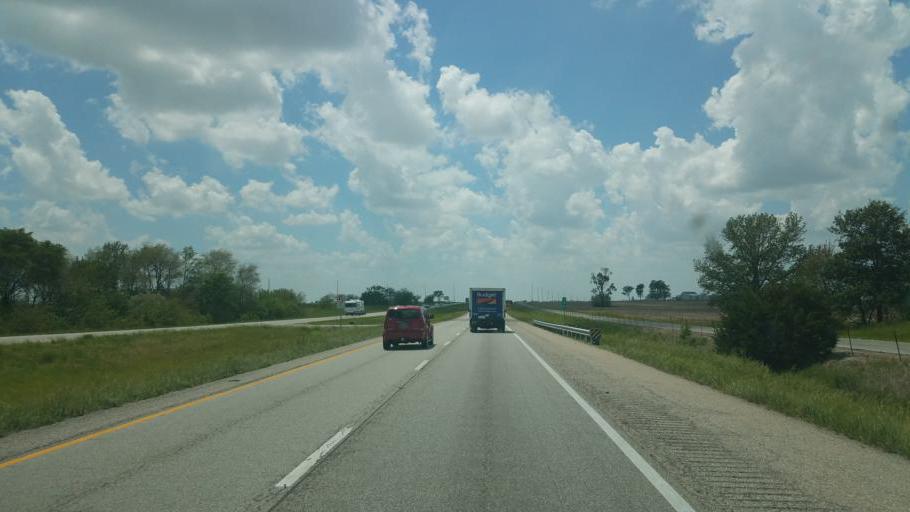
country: US
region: Illinois
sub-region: Madison County
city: Highland
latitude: 38.8231
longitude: -89.5572
